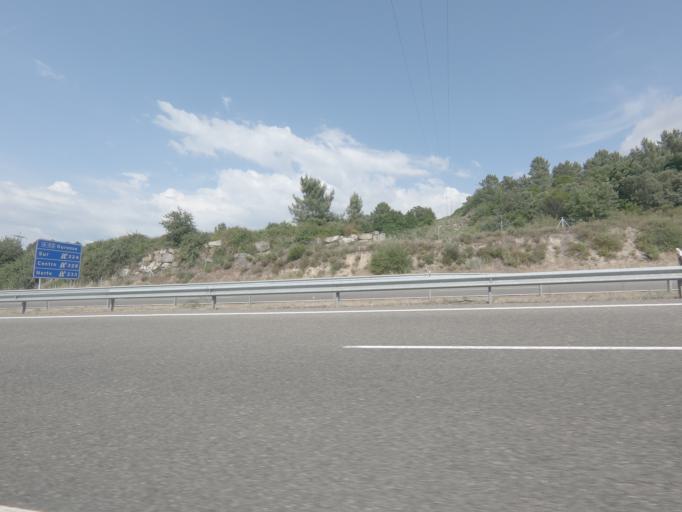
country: ES
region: Galicia
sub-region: Provincia de Ourense
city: Ourense
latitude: 42.2792
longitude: -7.8725
